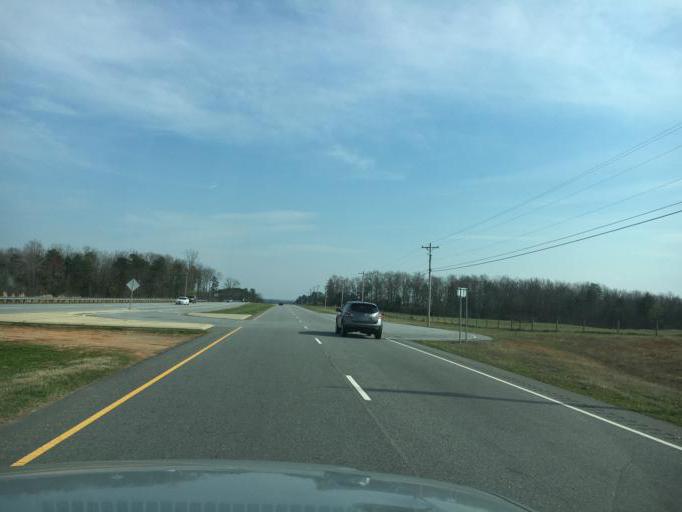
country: US
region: North Carolina
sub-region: Rutherford County
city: Forest City
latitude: 35.2667
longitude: -81.8888
